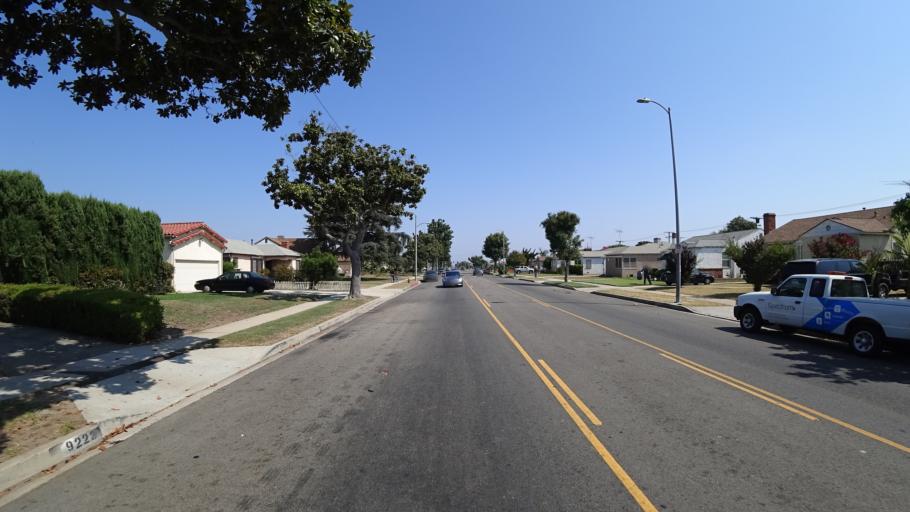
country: US
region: California
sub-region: Los Angeles County
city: Westmont
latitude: 33.9533
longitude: -118.3178
